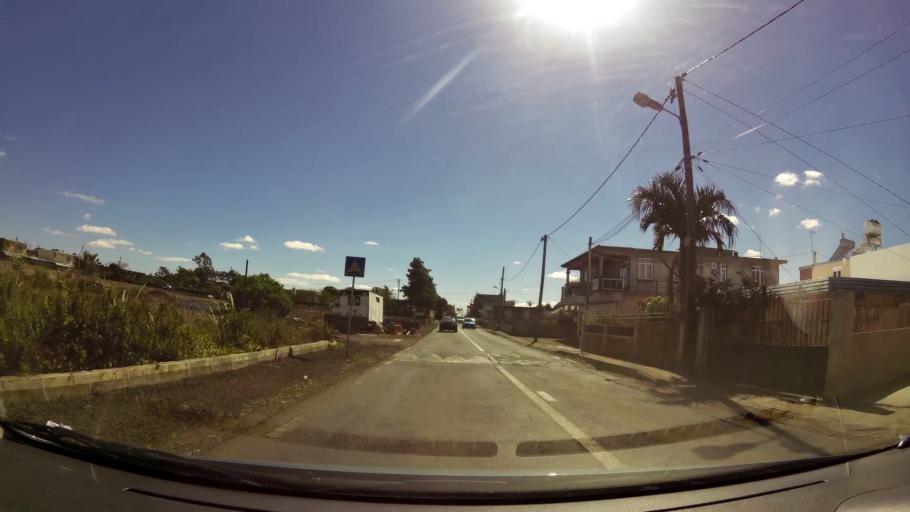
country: MU
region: Plaines Wilhems
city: Vacoas
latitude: -20.3289
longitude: 57.4863
